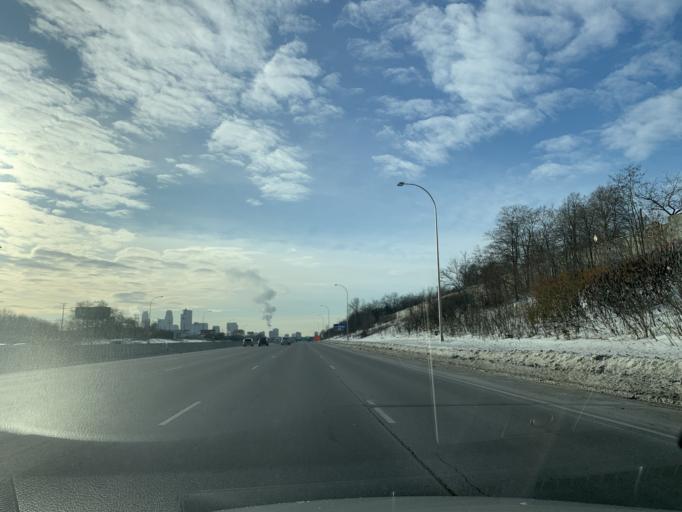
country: US
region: Minnesota
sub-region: Anoka County
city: Columbia Heights
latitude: 45.0126
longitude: -93.2828
